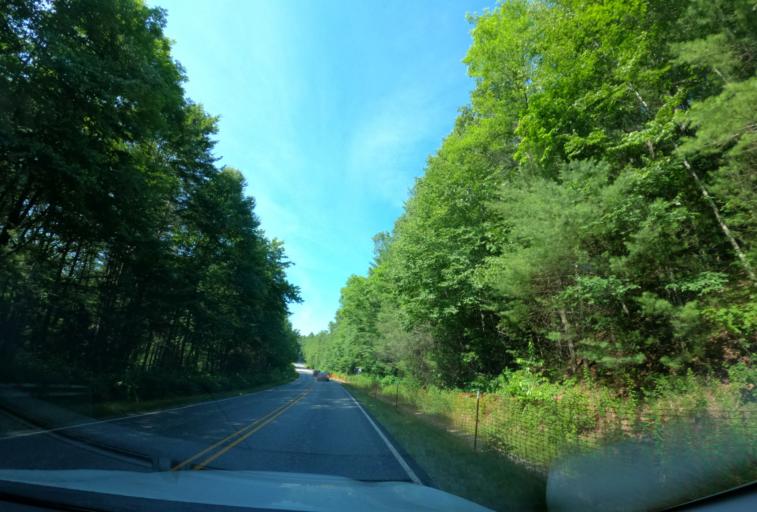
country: US
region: North Carolina
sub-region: Transylvania County
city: Brevard
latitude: 35.2006
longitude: -82.6198
